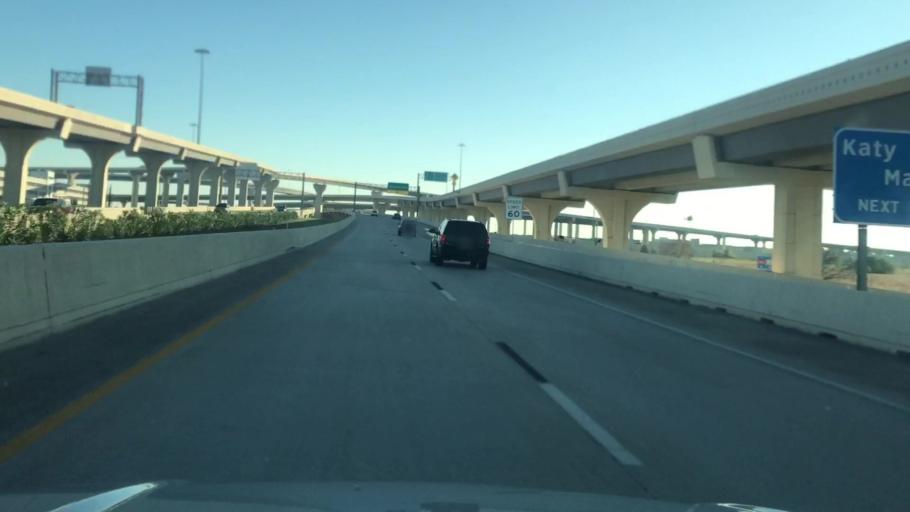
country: US
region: Texas
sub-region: Harris County
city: Katy
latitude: 29.7905
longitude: -95.7770
